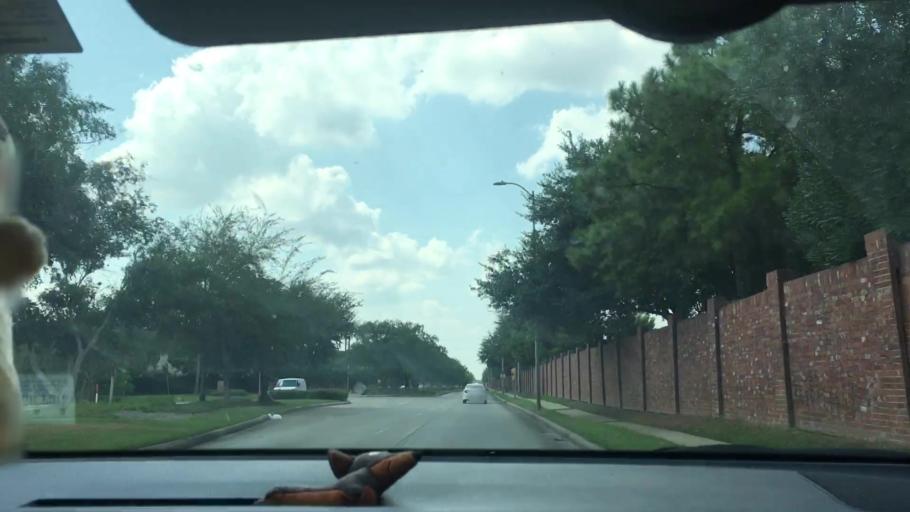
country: US
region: Texas
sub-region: Harris County
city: Bunker Hill Village
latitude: 29.7252
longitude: -95.5717
